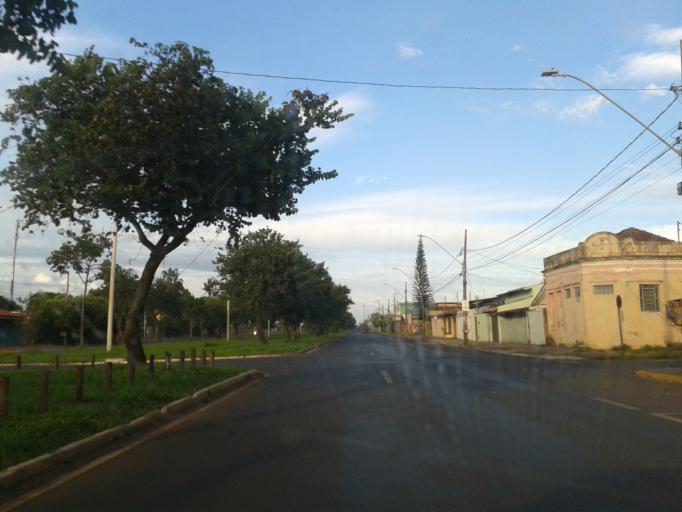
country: BR
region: Minas Gerais
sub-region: Araguari
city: Araguari
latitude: -18.6408
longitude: -48.1946
